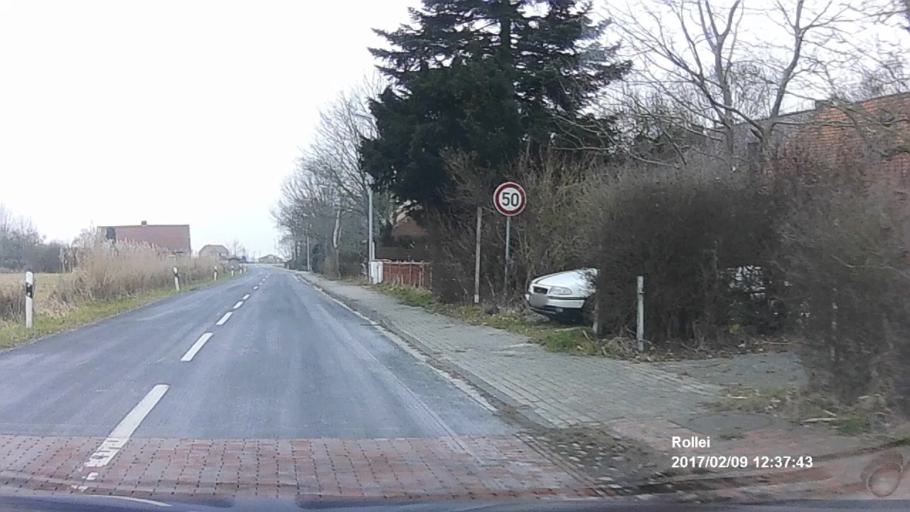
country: DE
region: Lower Saxony
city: Weener
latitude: 53.1994
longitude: 7.4039
